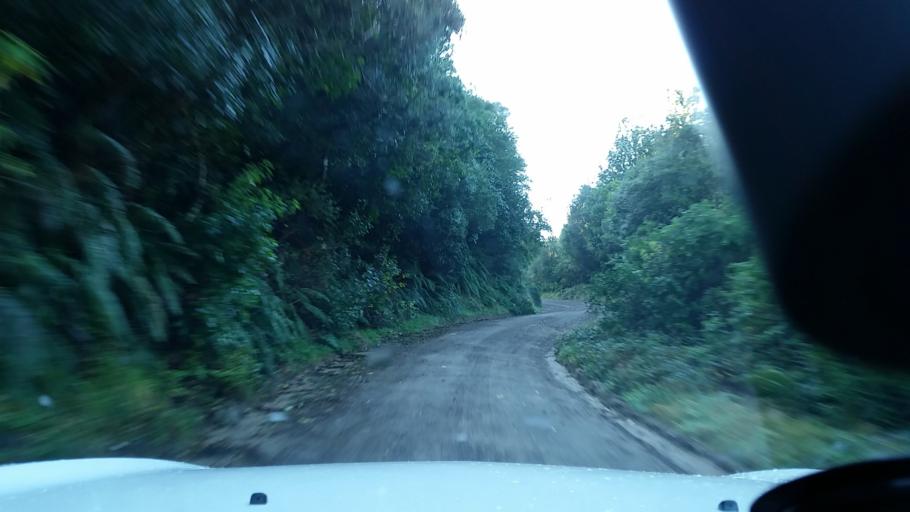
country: NZ
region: Bay of Plenty
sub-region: Kawerau District
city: Kawerau
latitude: -38.0021
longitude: 176.6017
